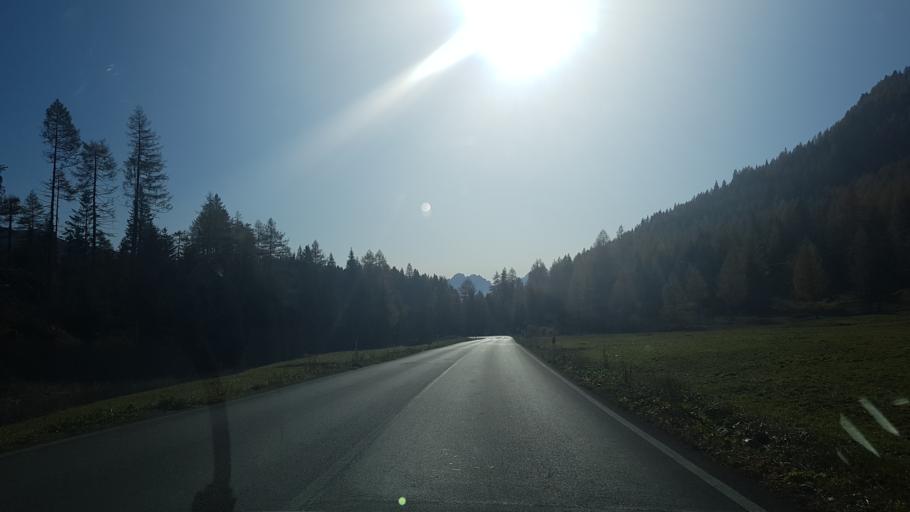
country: IT
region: Trentino-Alto Adige
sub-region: Bolzano
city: Sesto
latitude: 46.6514
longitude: 12.4263
